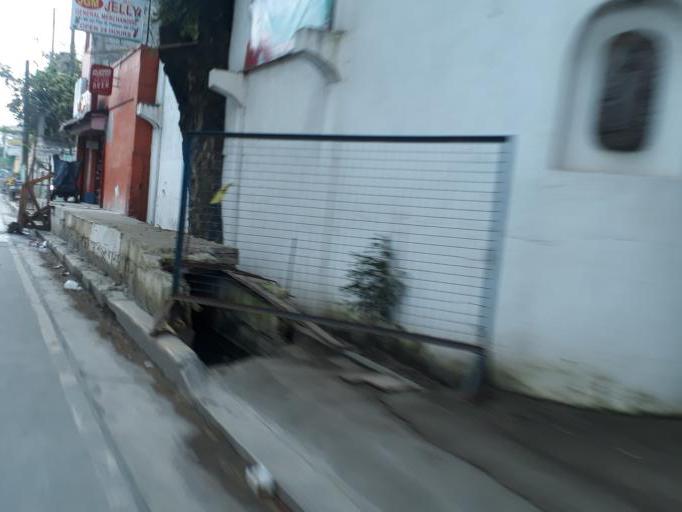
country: PH
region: Central Luzon
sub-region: Province of Bulacan
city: Obando
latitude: 14.7036
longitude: 120.9487
